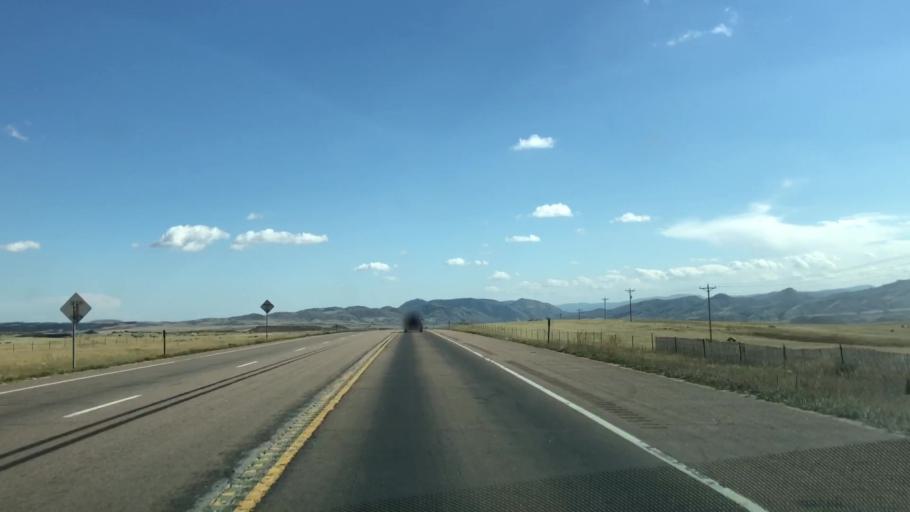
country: US
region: Colorado
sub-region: Larimer County
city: Laporte
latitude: 40.8519
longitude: -105.2567
